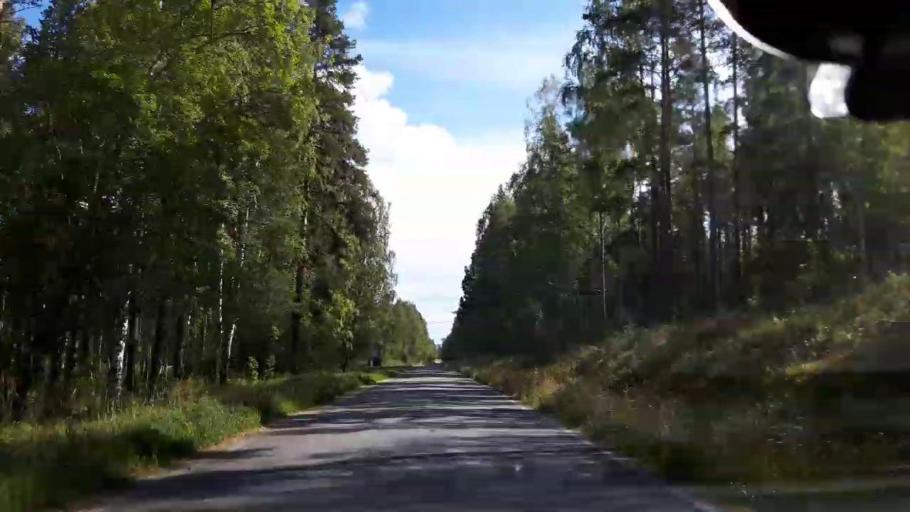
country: SE
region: Jaemtland
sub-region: Braecke Kommun
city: Braecke
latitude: 63.2197
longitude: 15.3170
